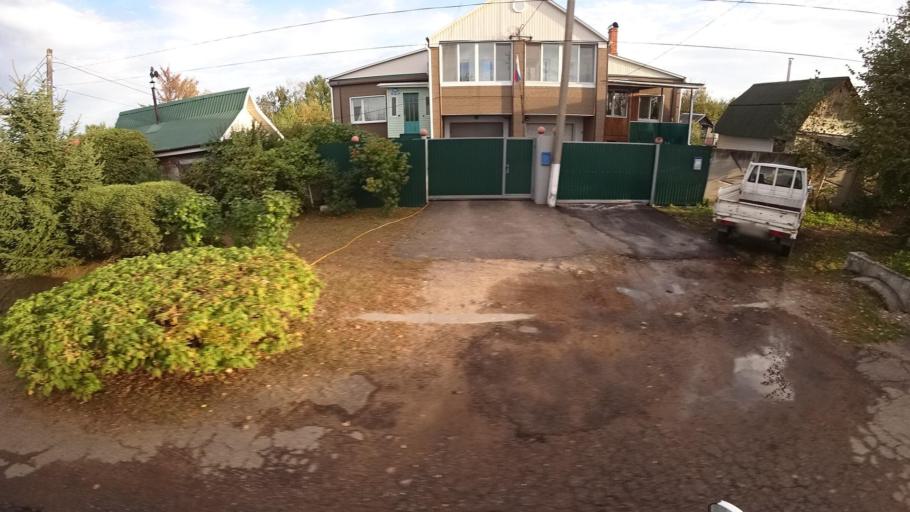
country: RU
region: Primorskiy
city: Yakovlevka
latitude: 44.4288
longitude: 133.4752
